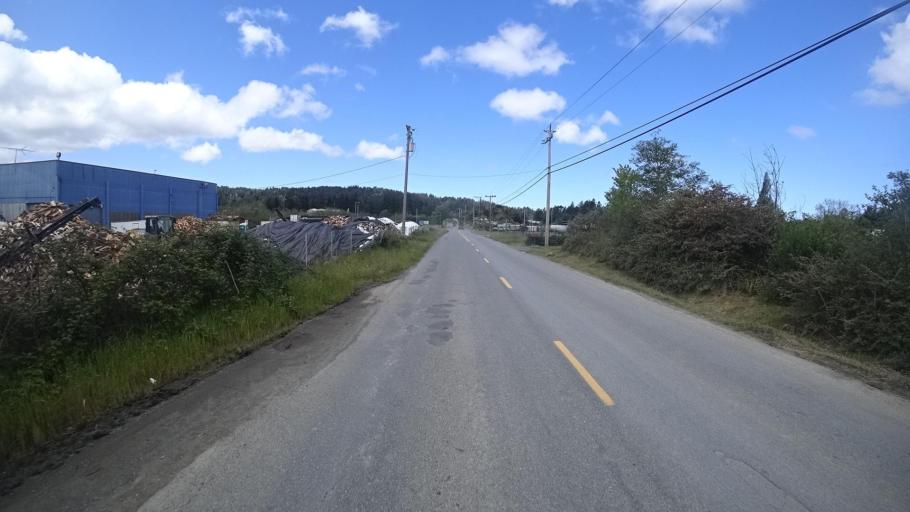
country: US
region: California
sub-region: Humboldt County
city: Blue Lake
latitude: 40.9001
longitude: -124.0155
